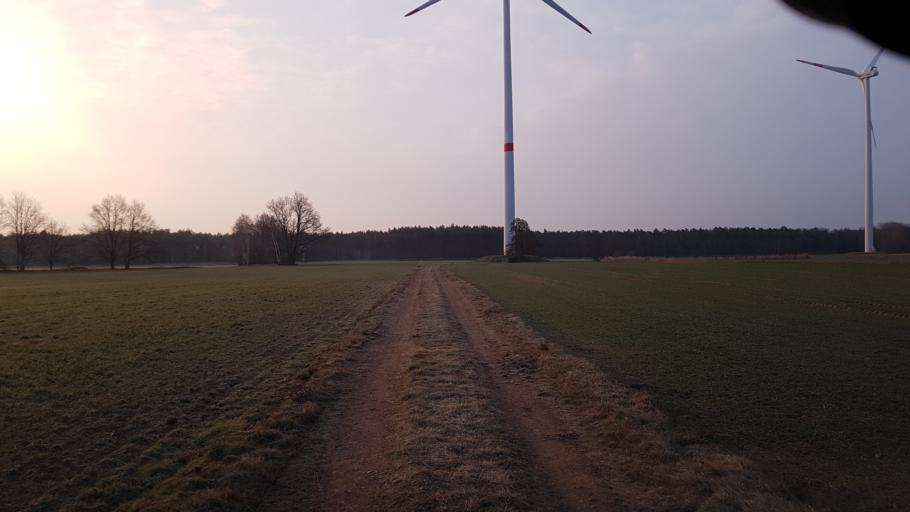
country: DE
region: Brandenburg
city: Falkenberg
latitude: 51.5707
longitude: 13.3030
